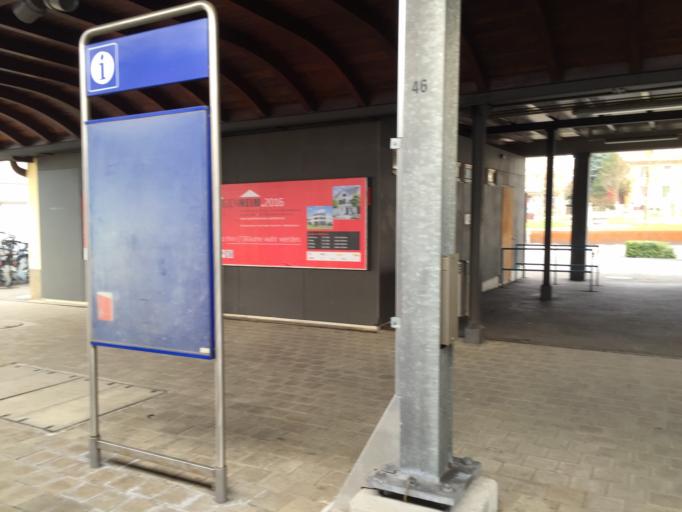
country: CH
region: Solothurn
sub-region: Bezirk Lebern
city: Grenchen
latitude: 47.1886
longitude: 7.3980
